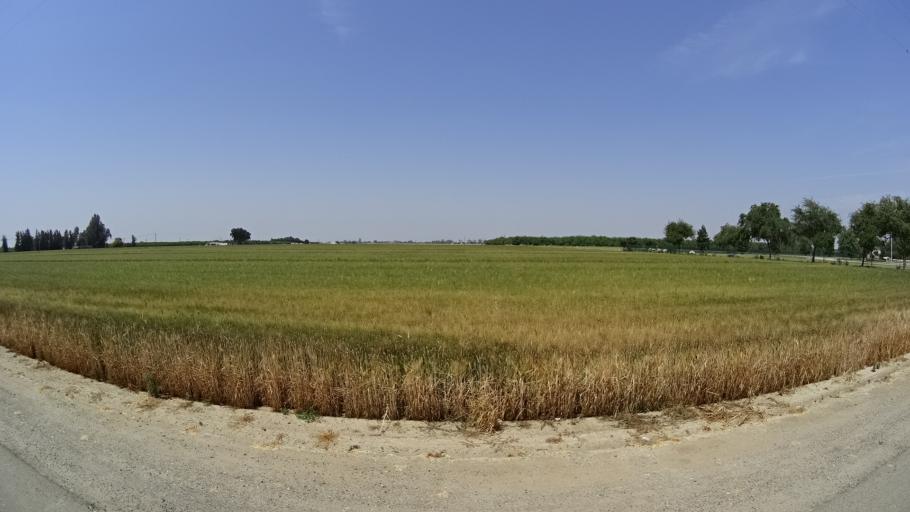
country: US
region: California
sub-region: Kings County
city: Lemoore
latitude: 36.3312
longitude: -119.7808
